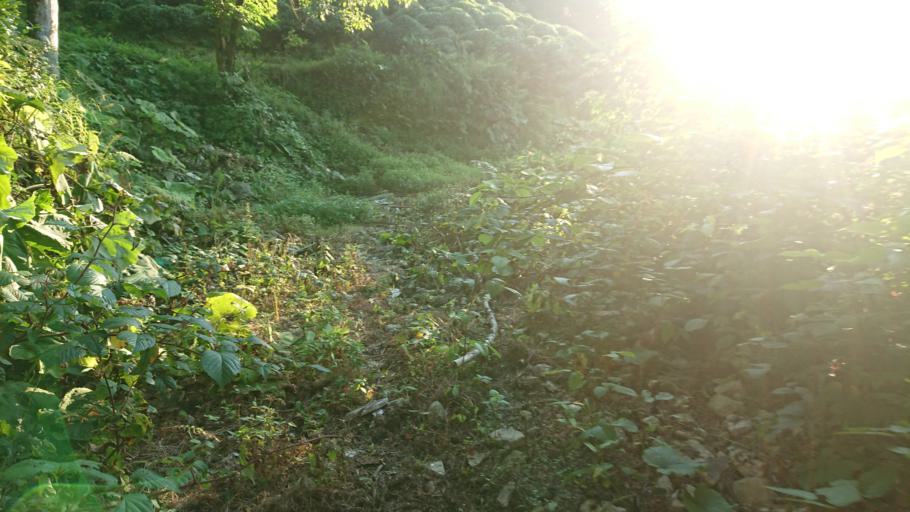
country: TR
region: Rize
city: Rize
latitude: 40.9792
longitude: 40.4999
